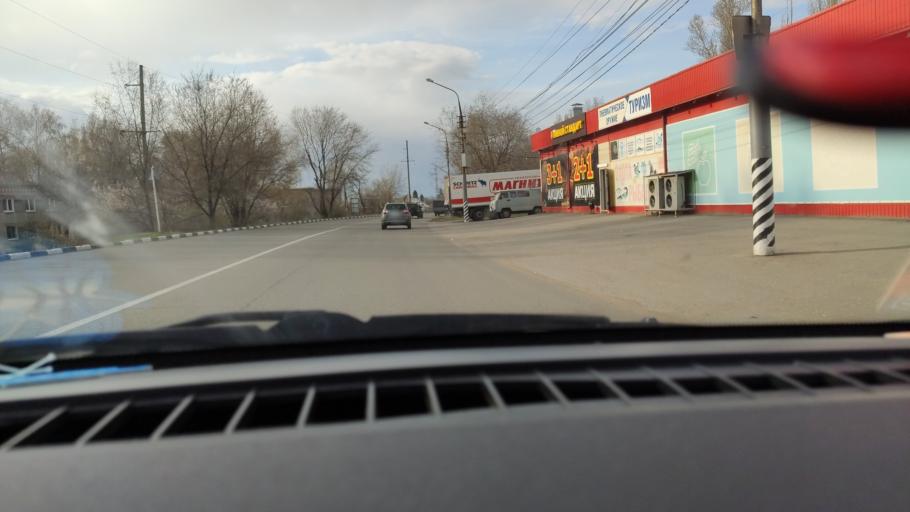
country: RU
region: Saratov
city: Privolzhskiy
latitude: 51.3935
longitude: 46.0343
